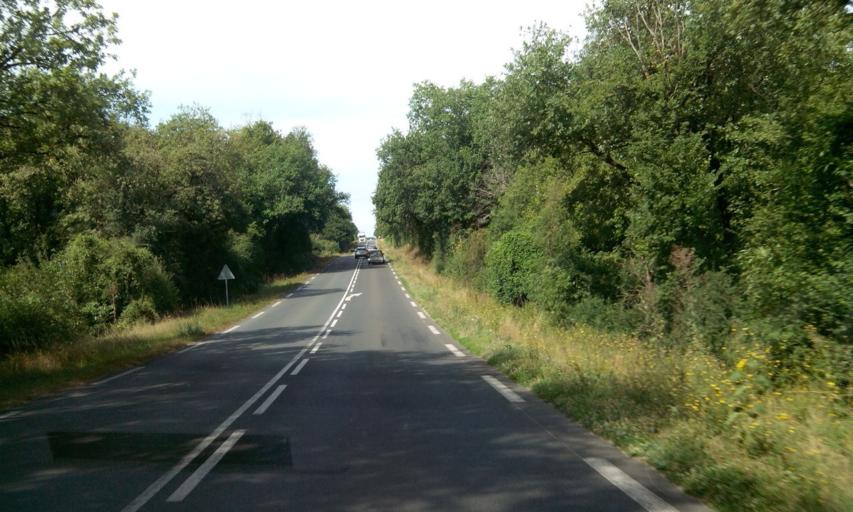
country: FR
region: Poitou-Charentes
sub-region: Departement de la Vienne
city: Chaunay
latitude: 46.1422
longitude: 0.2121
